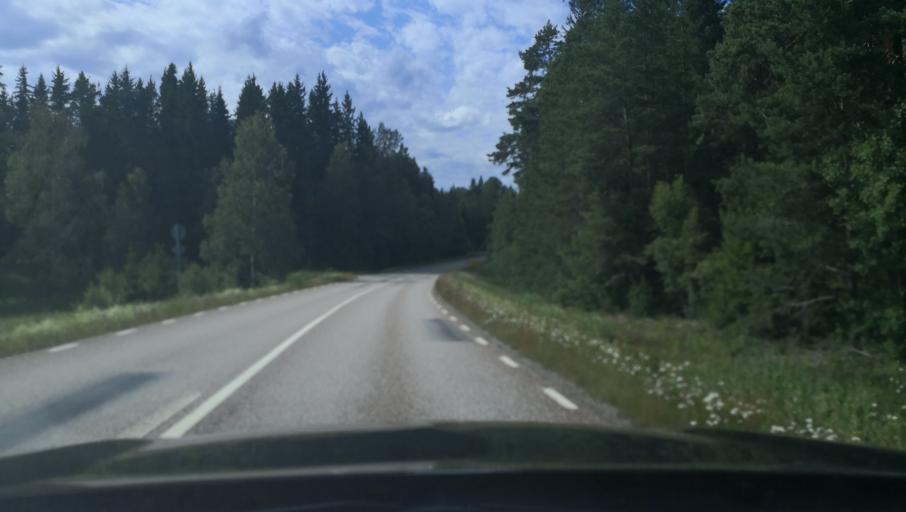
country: SE
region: Dalarna
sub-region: Avesta Kommun
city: Avesta
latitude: 59.9732
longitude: 16.1516
